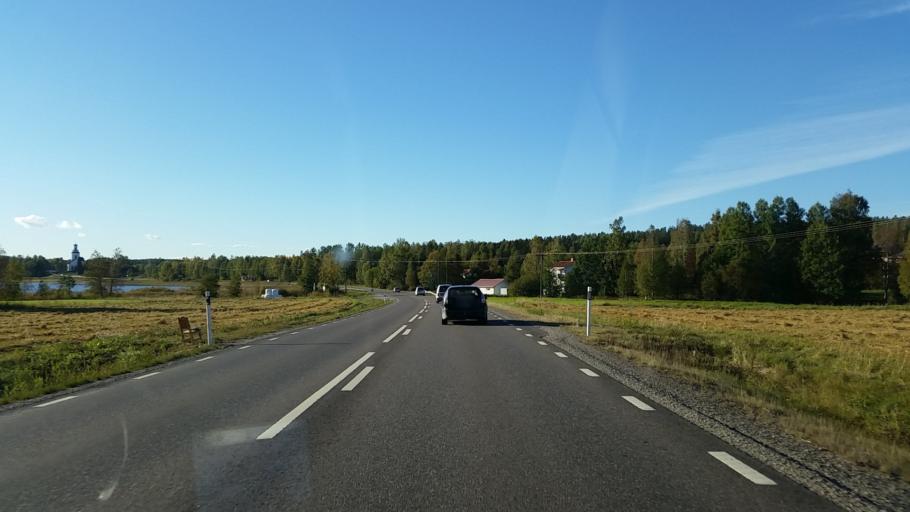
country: SE
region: Gaevleborg
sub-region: Hudiksvalls Kommun
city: Sorforsa
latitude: 61.7310
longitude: 16.9602
